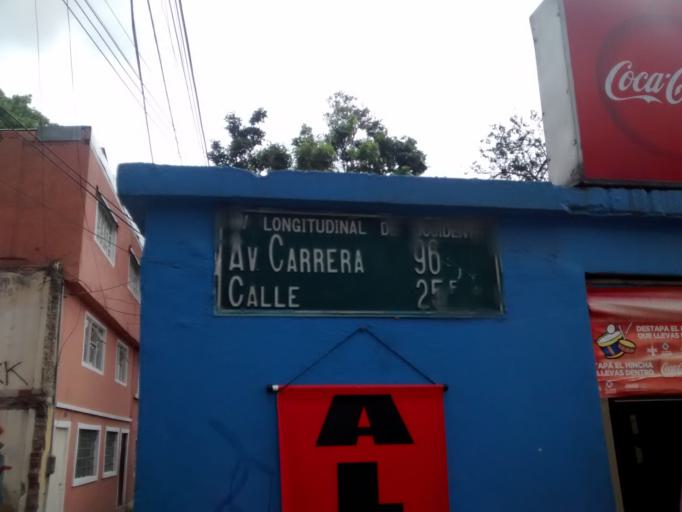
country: CO
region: Bogota D.C.
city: Bogota
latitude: 4.6828
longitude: -74.1261
